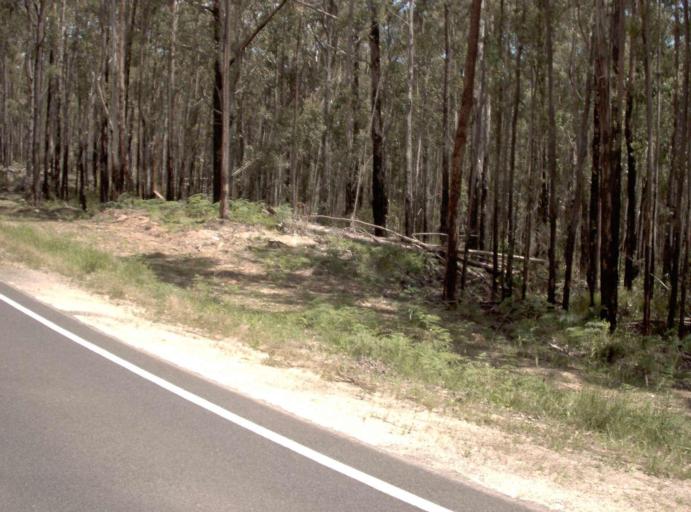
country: AU
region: New South Wales
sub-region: Bombala
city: Bombala
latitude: -37.5635
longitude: 149.2508
